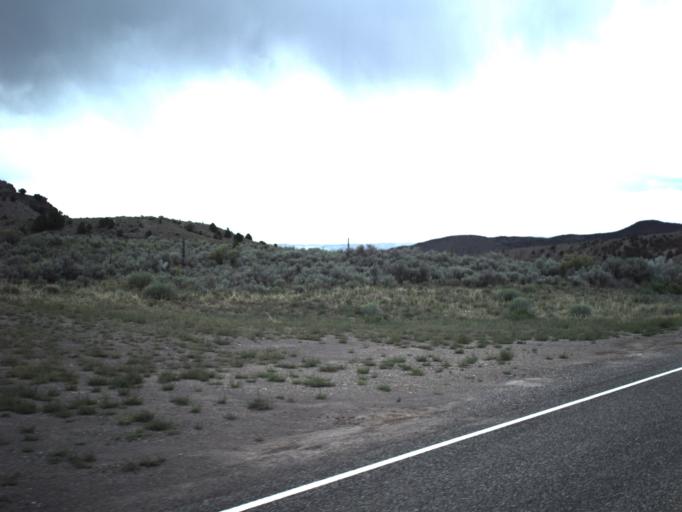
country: US
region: Utah
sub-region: Piute County
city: Junction
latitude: 38.1799
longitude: -112.0791
